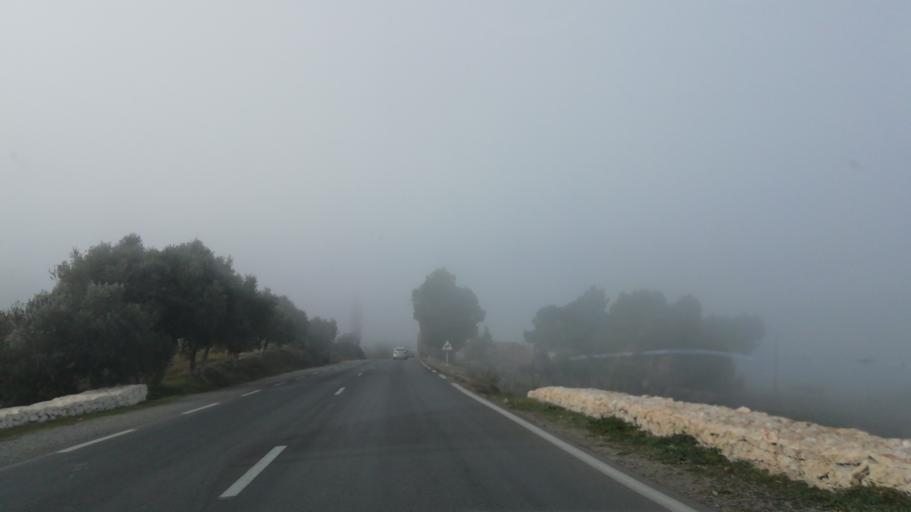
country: DZ
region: Mascara
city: Mascara
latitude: 35.5266
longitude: 0.3416
